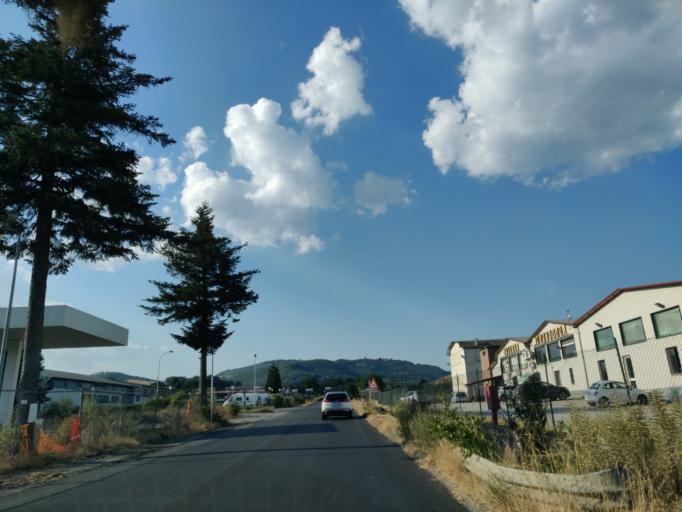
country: IT
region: Latium
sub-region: Provincia di Viterbo
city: Acquapendente
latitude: 42.7670
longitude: 11.8561
